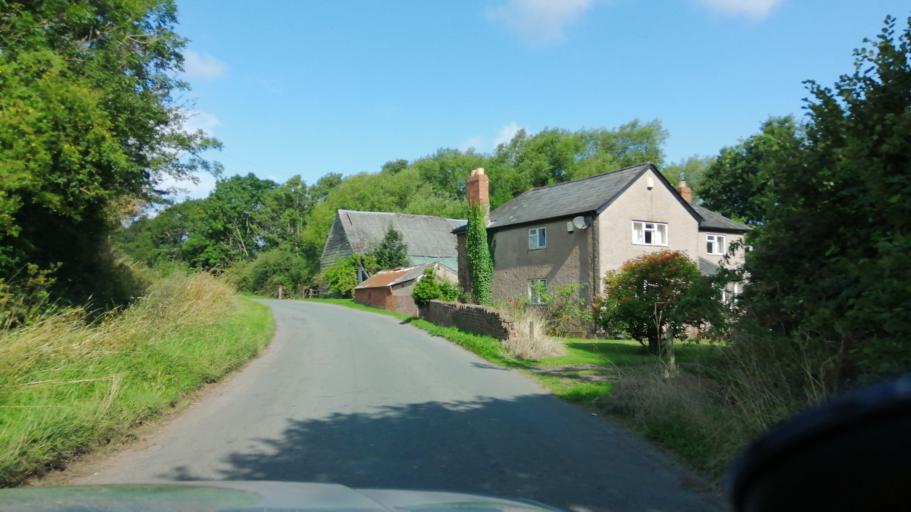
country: GB
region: England
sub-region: Herefordshire
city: Madley
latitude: 52.0533
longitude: -2.8547
